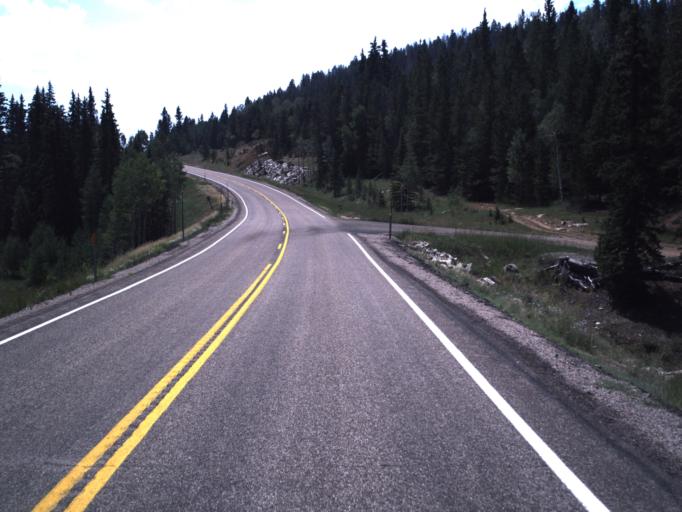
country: US
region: Utah
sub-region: Uintah County
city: Maeser
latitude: 40.7077
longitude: -109.4944
